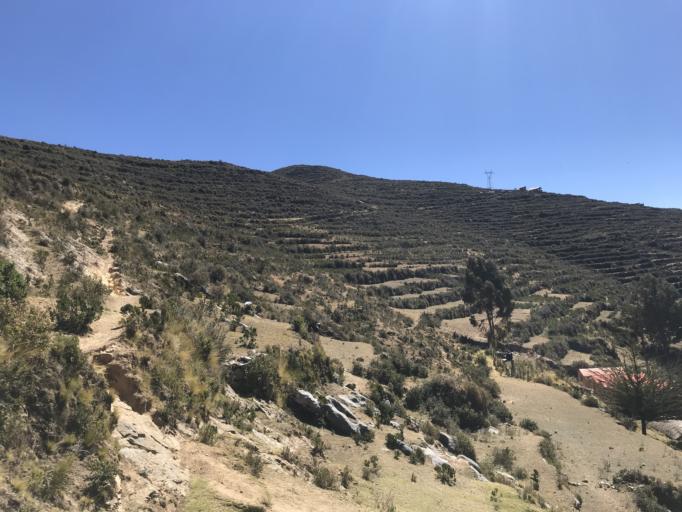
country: BO
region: La Paz
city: Yumani
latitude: -16.0487
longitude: -69.1446
